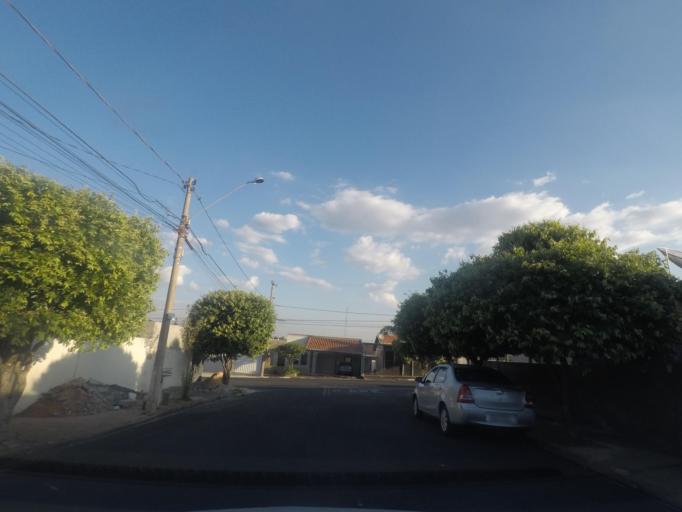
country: BR
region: Sao Paulo
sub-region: Sumare
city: Sumare
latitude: -22.8142
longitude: -47.2831
